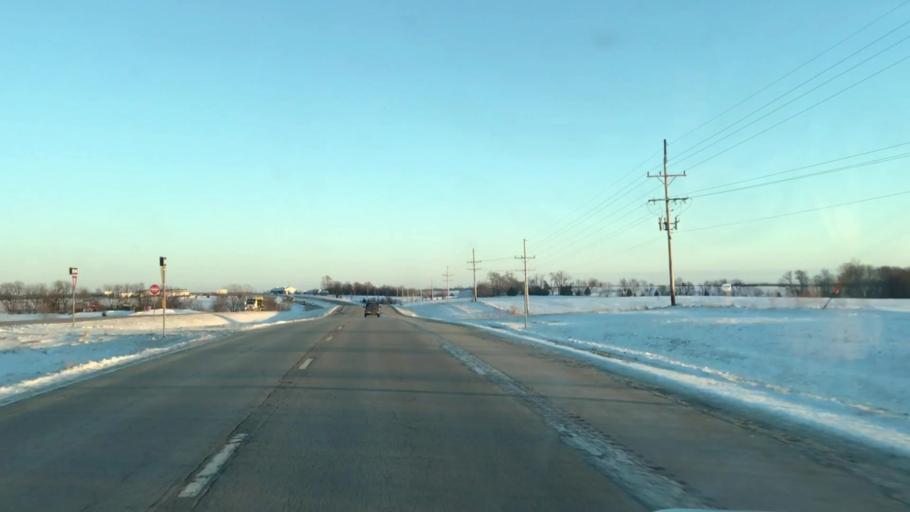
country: US
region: Missouri
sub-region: Clinton County
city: Cameron
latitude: 39.7591
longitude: -94.3472
